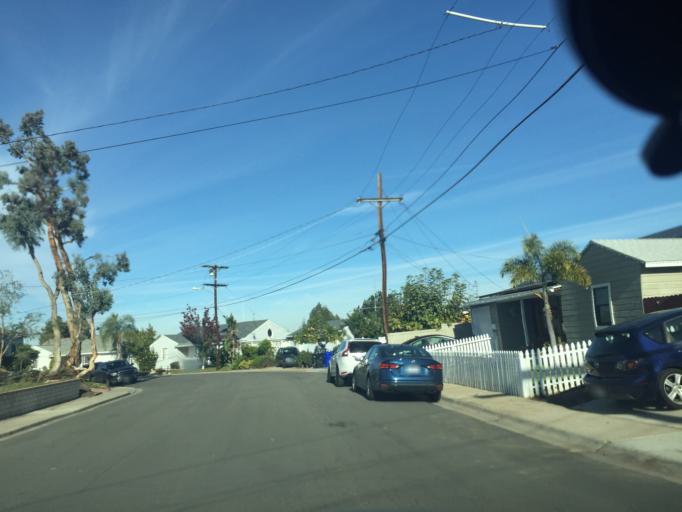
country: US
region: California
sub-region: San Diego County
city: Lemon Grove
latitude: 32.7662
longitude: -117.0811
